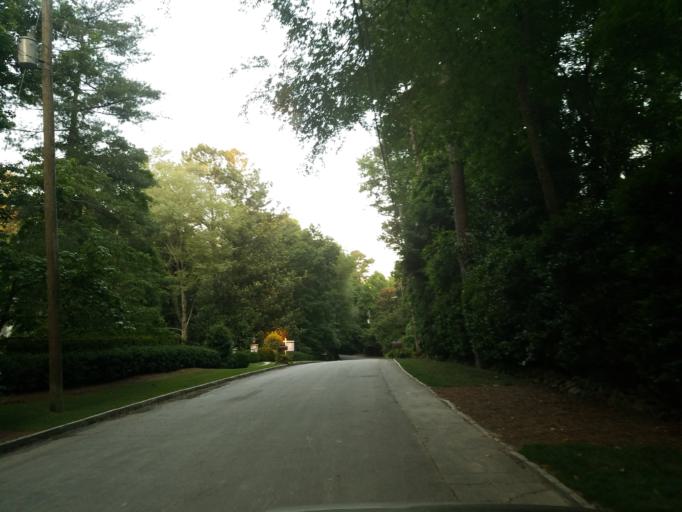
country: US
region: Georgia
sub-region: Cobb County
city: Vinings
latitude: 33.8545
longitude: -84.4510
